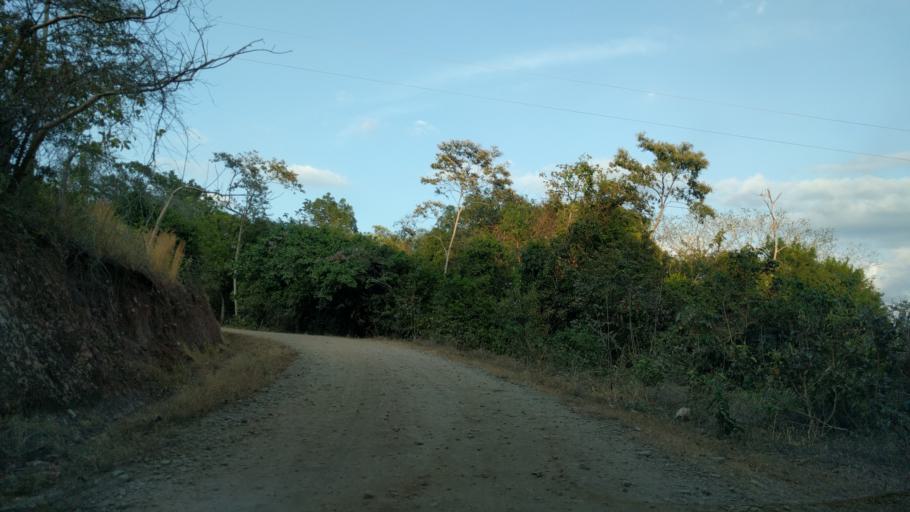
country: CR
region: Puntarenas
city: Esparza
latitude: 10.0230
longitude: -84.6993
